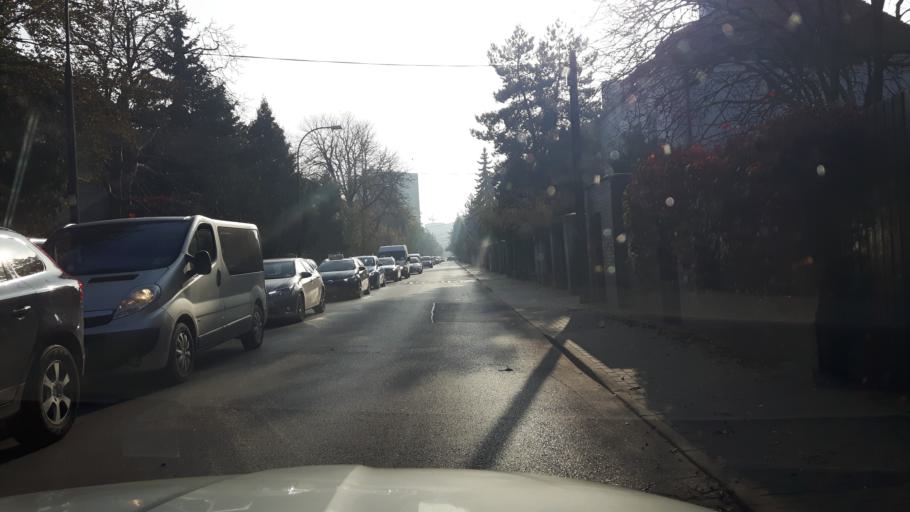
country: PL
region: Masovian Voivodeship
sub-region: Warszawa
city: Ochota
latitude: 52.1963
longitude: 20.9926
